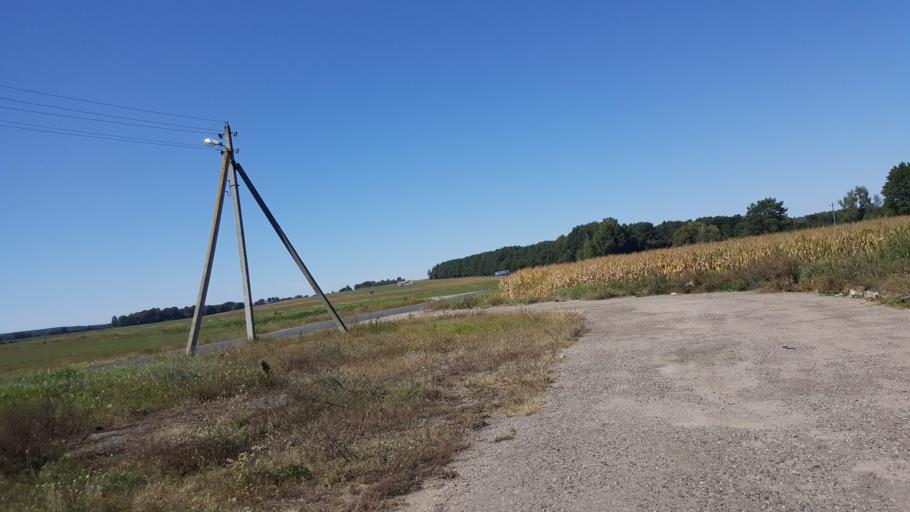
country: PL
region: Lublin Voivodeship
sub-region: Powiat bialski
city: Terespol
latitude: 52.2156
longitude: 23.5082
